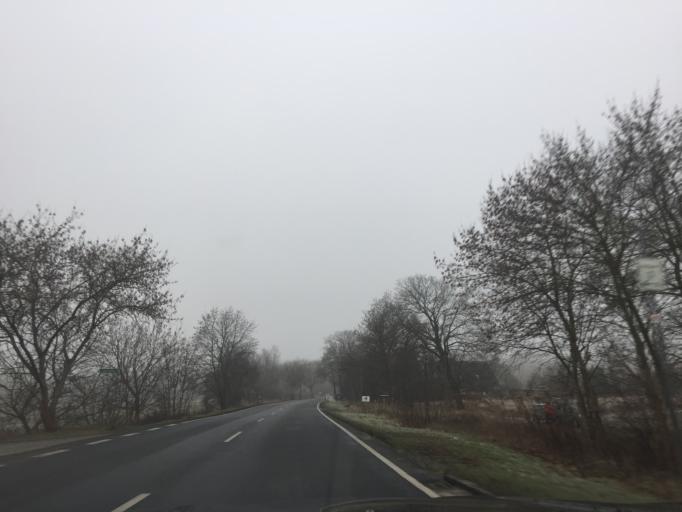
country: DE
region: Brandenburg
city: Hennigsdorf
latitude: 52.6381
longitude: 13.1487
